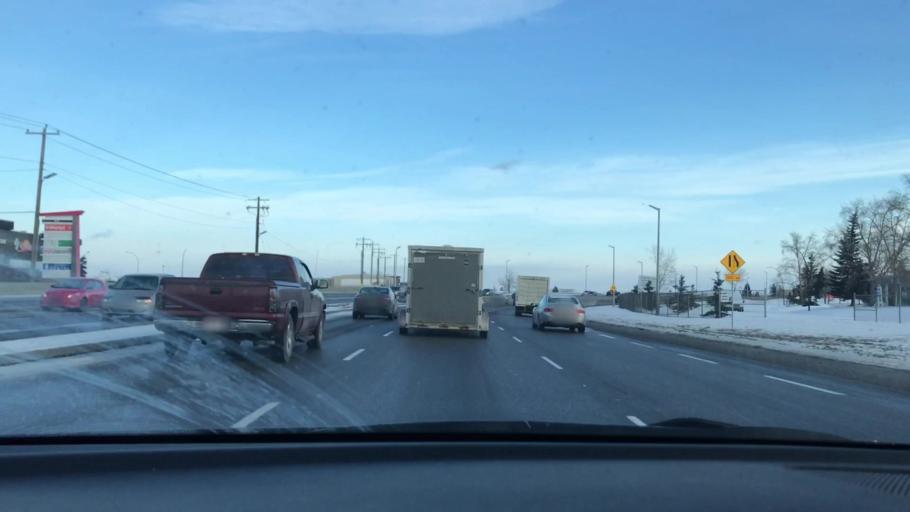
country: CA
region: Alberta
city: Calgary
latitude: 51.0960
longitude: -114.0317
